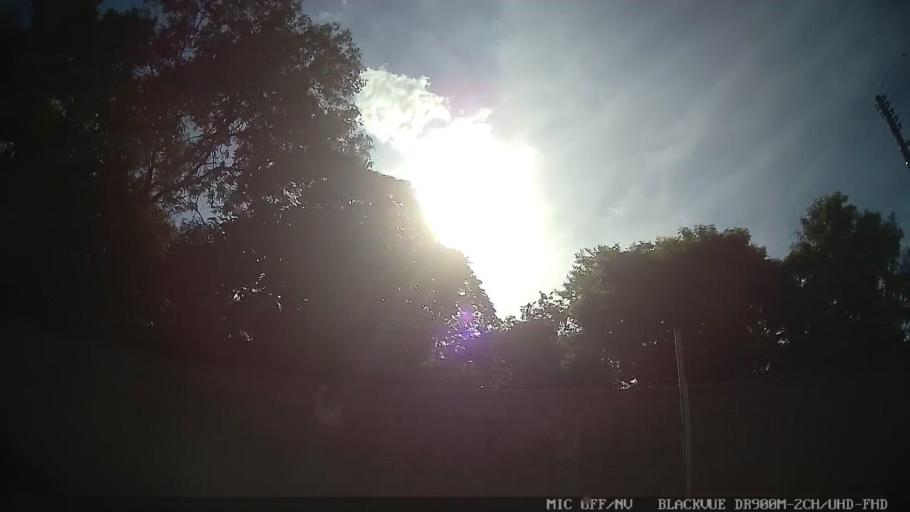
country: BR
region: Sao Paulo
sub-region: Jaguariuna
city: Jaguariuna
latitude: -22.6365
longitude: -47.0554
